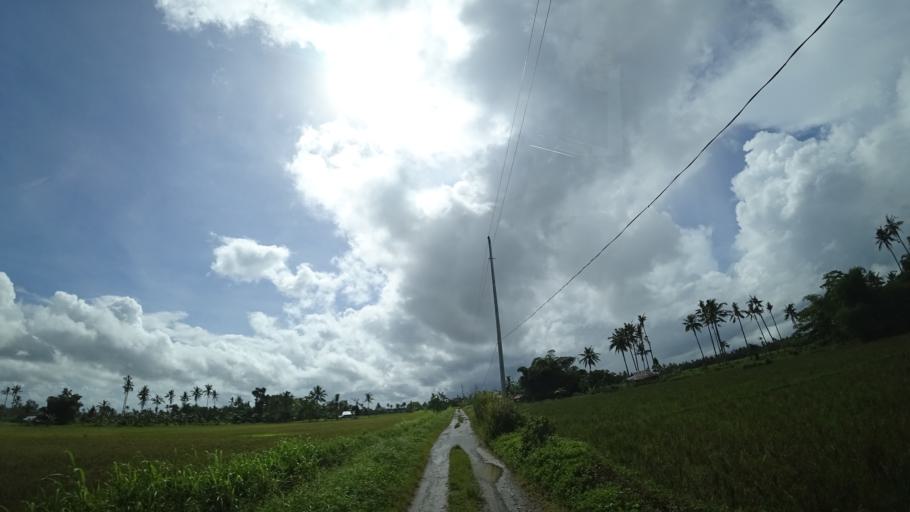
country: PH
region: Eastern Visayas
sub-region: Province of Leyte
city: Cabacungan
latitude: 10.9157
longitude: 124.9779
